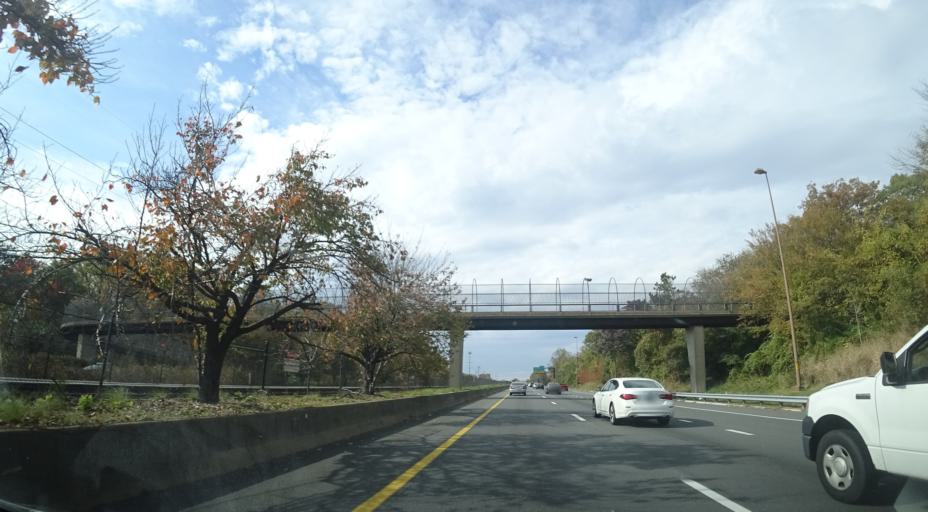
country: US
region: Virginia
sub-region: Fairfax County
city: Seven Corners
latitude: 38.8836
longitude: -77.1493
